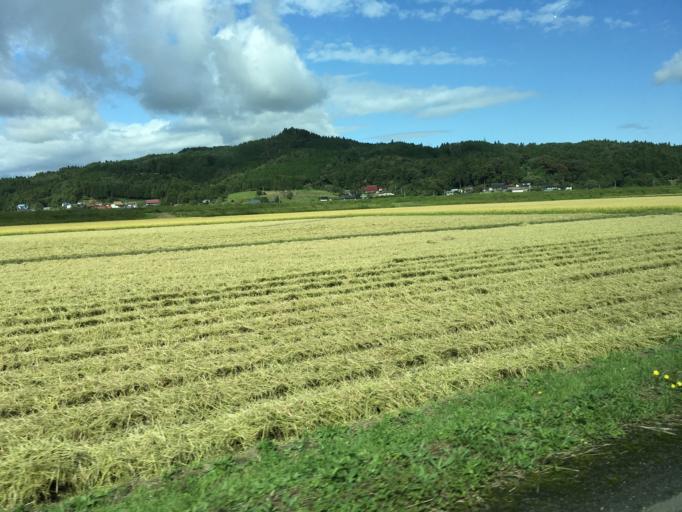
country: JP
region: Iwate
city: Ichinoseki
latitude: 38.8421
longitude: 141.2735
